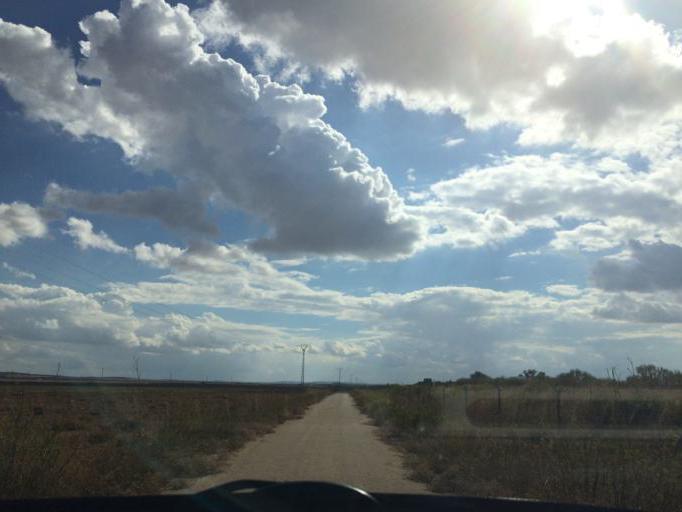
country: ES
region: Castille-La Mancha
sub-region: Provincia de Albacete
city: Albacete
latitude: 38.9572
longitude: -1.8214
